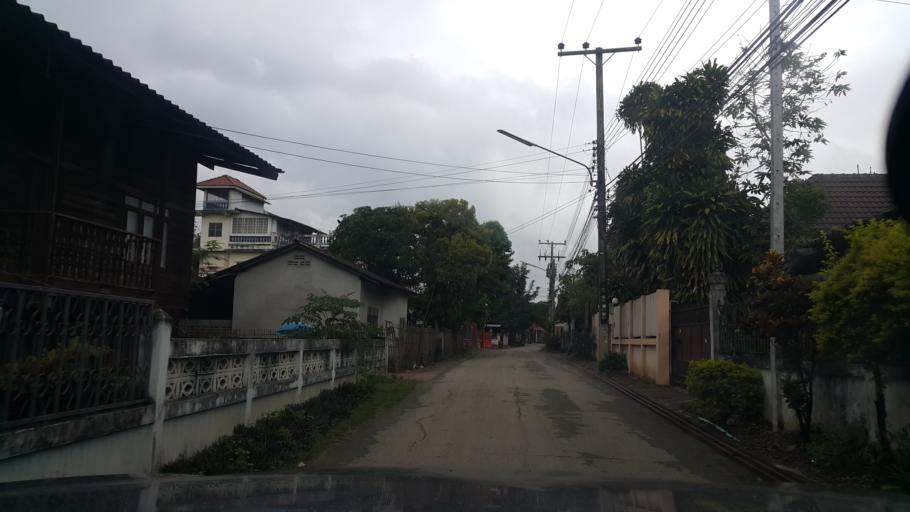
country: TH
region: Chiang Mai
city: Mae On
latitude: 18.7712
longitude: 99.2572
